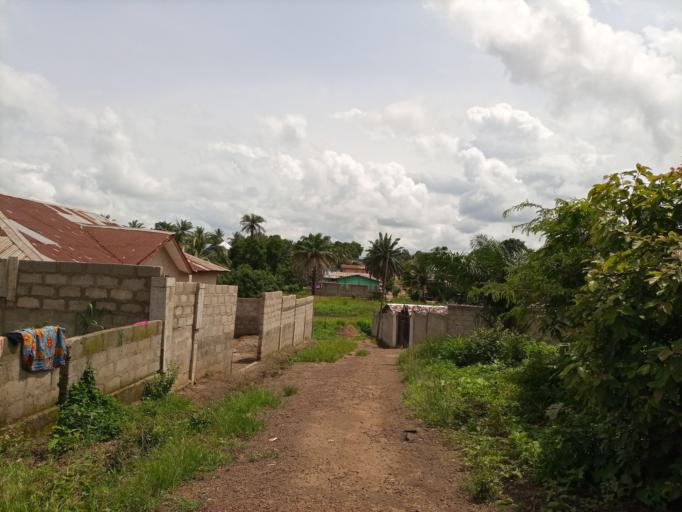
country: SL
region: Southern Province
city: Bo
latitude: 7.9595
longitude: -11.7588
